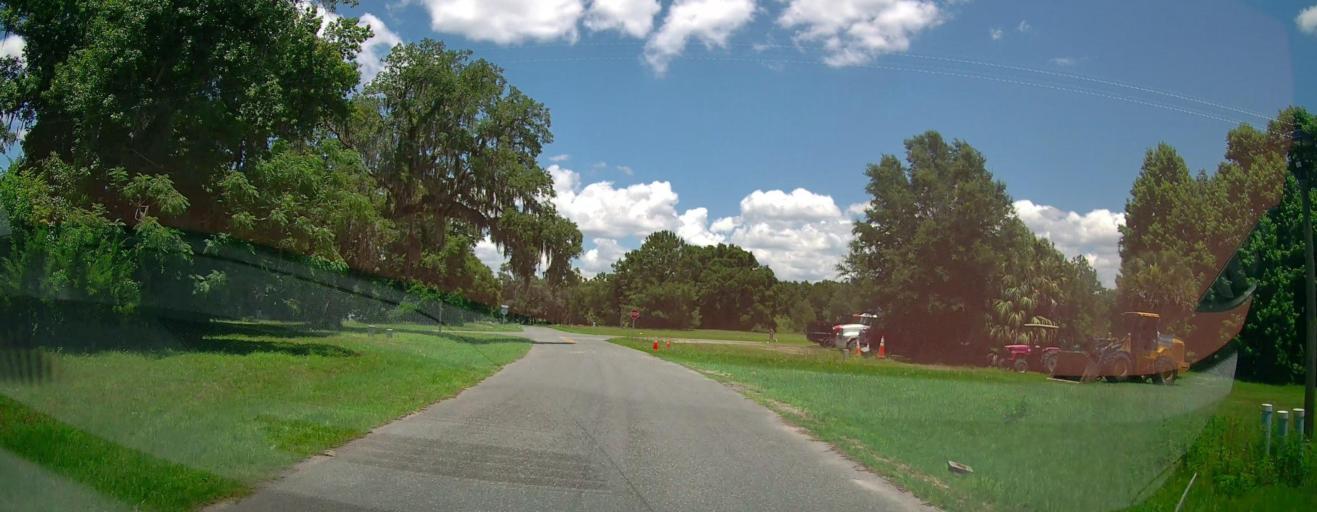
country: US
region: Florida
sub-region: Marion County
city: Belleview
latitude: 29.0903
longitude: -82.0742
